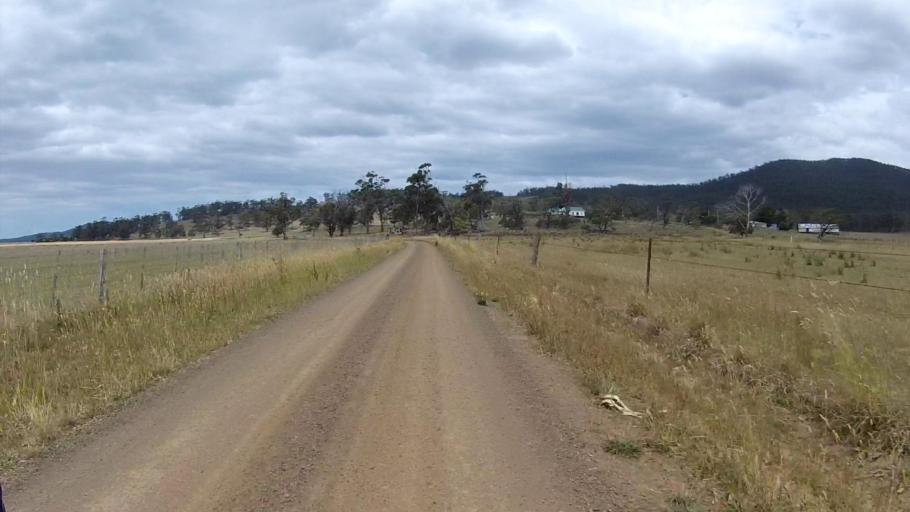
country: AU
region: Tasmania
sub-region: Sorell
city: Sorell
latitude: -42.6581
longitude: 147.9402
